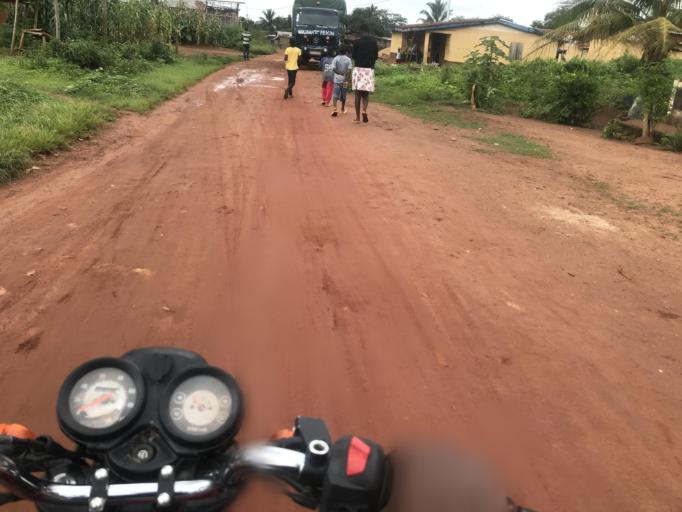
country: SL
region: Eastern Province
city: Buedu
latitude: 8.4616
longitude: -10.3356
